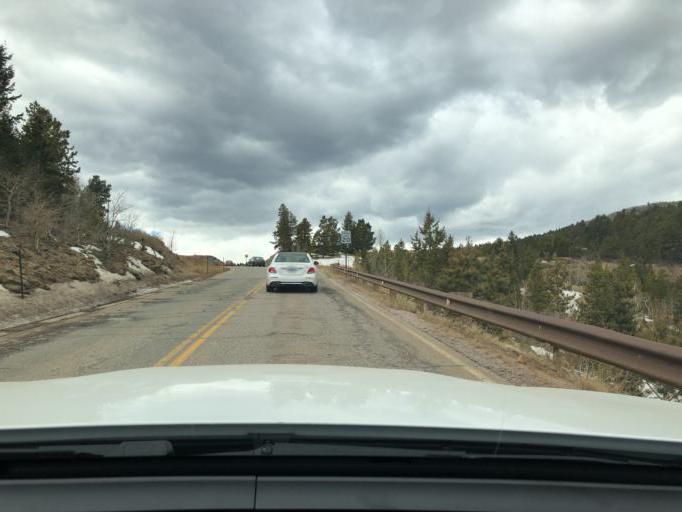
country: US
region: Colorado
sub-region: Gilpin County
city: Central City
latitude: 39.7918
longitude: -105.5145
